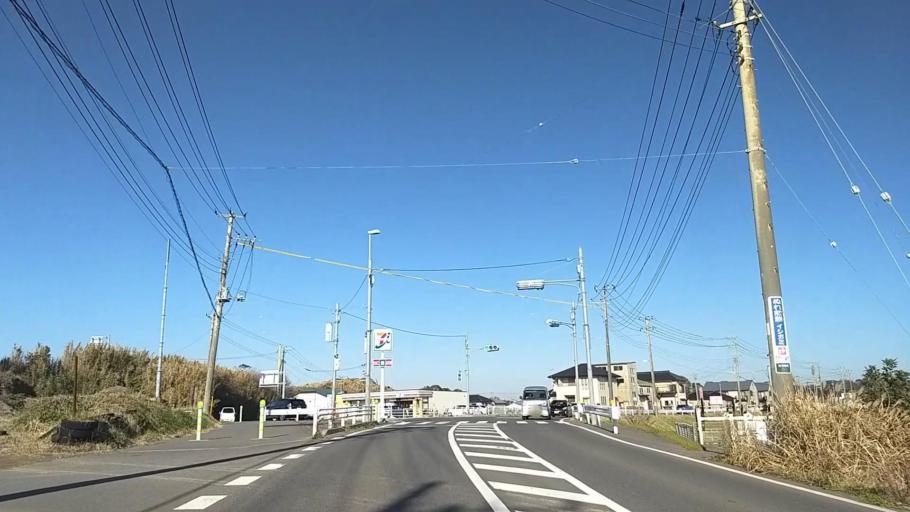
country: JP
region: Chiba
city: Hasaki
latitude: 35.7111
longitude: 140.8412
